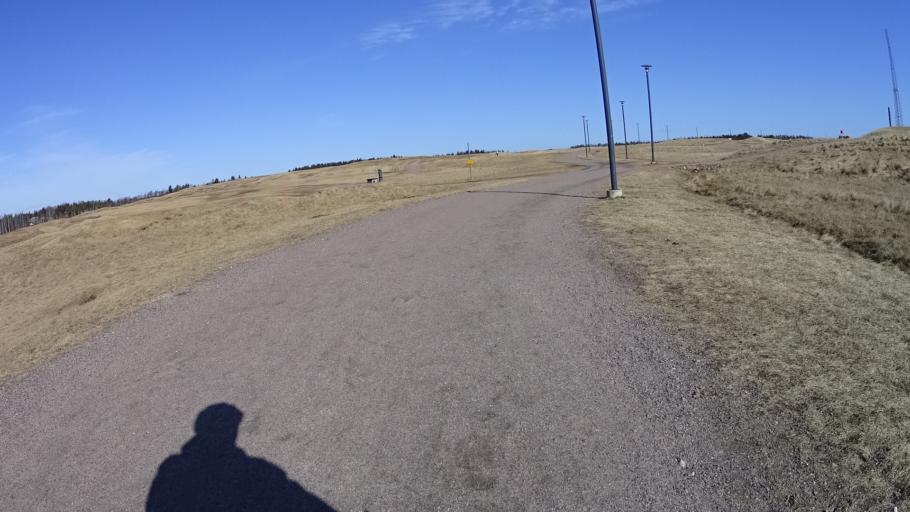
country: FI
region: Uusimaa
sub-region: Helsinki
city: Kilo
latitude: 60.1950
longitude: 24.7817
